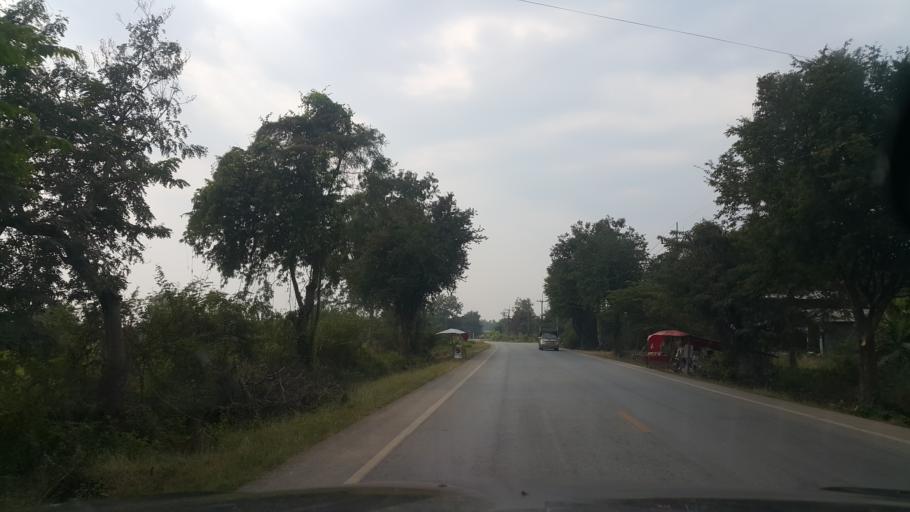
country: TH
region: Sukhothai
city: Si Samrong
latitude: 17.0977
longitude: 99.8850
